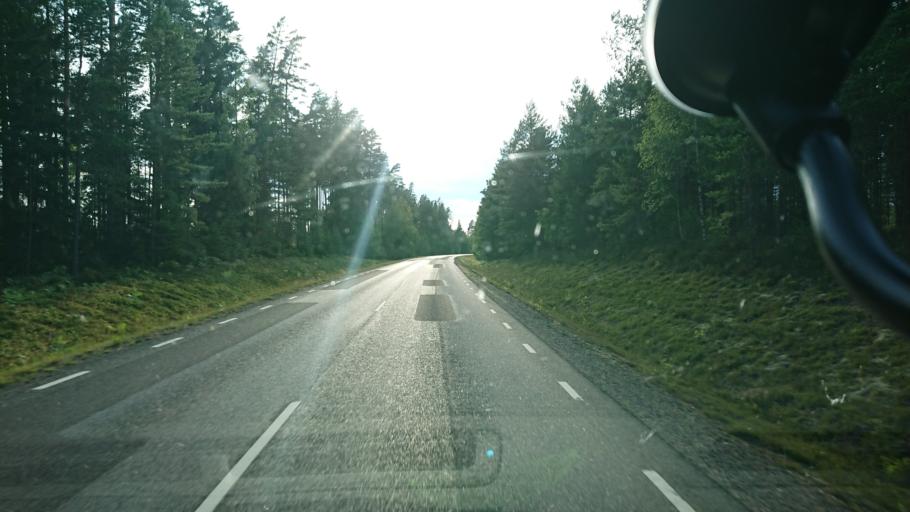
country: SE
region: Kronoberg
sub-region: Vaxjo Kommun
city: Braas
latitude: 57.0254
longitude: 14.9870
